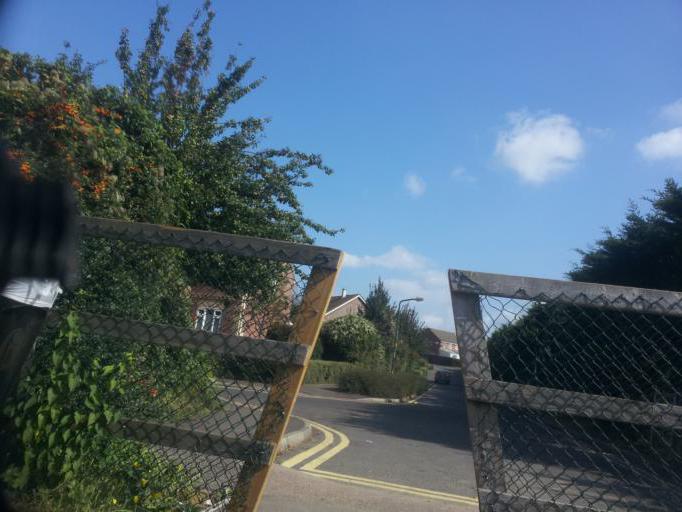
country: GB
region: England
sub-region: Medway
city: Rochester
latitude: 51.3974
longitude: 0.5036
